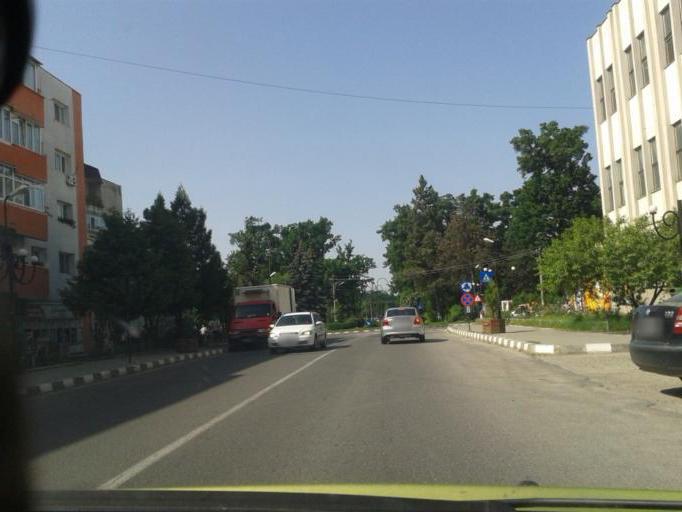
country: RO
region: Prahova
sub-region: Comuna Paulesti
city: Gageni
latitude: 45.0503
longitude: 25.9529
